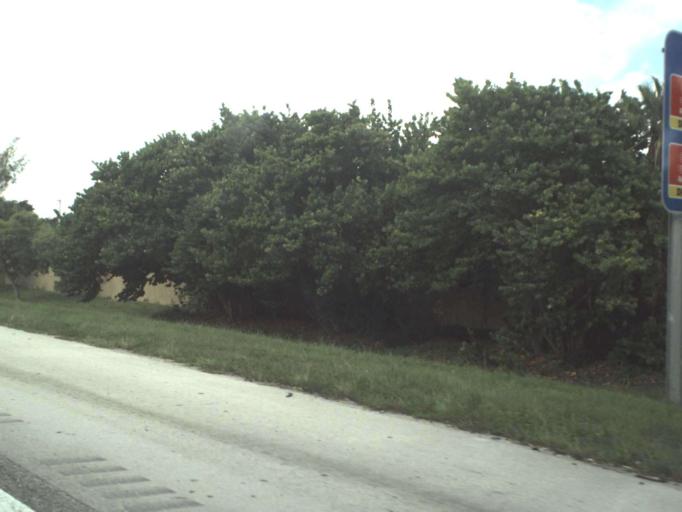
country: US
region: Florida
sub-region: Broward County
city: Tedder
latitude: 26.2875
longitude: -80.1248
